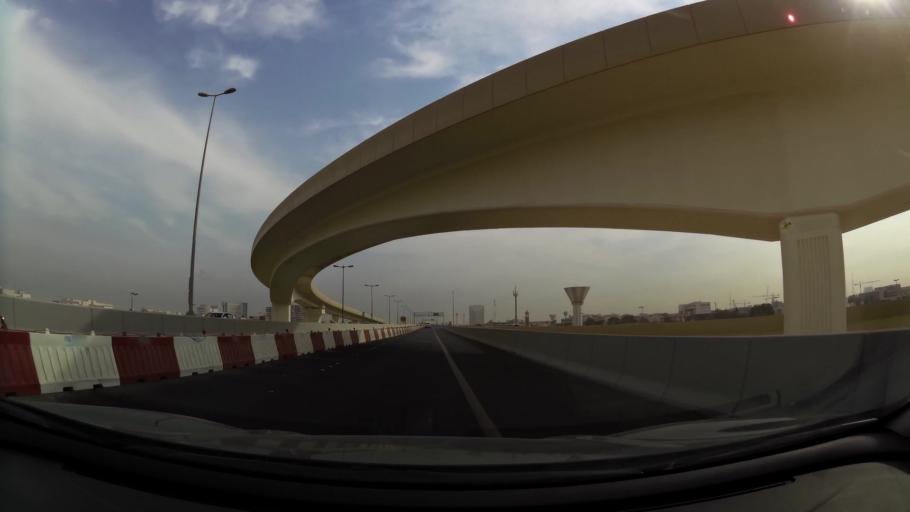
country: KW
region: Al Asimah
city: Ar Rabiyah
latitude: 29.3259
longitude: 47.8956
